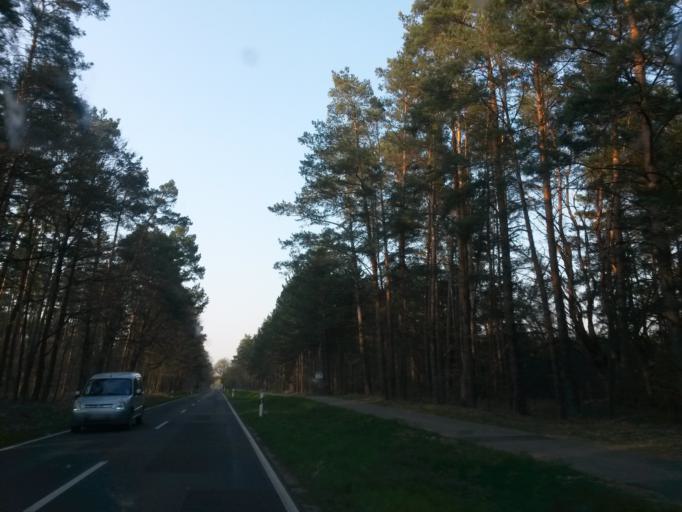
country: DE
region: Brandenburg
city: Rehfelde
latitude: 52.4744
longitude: 13.9090
